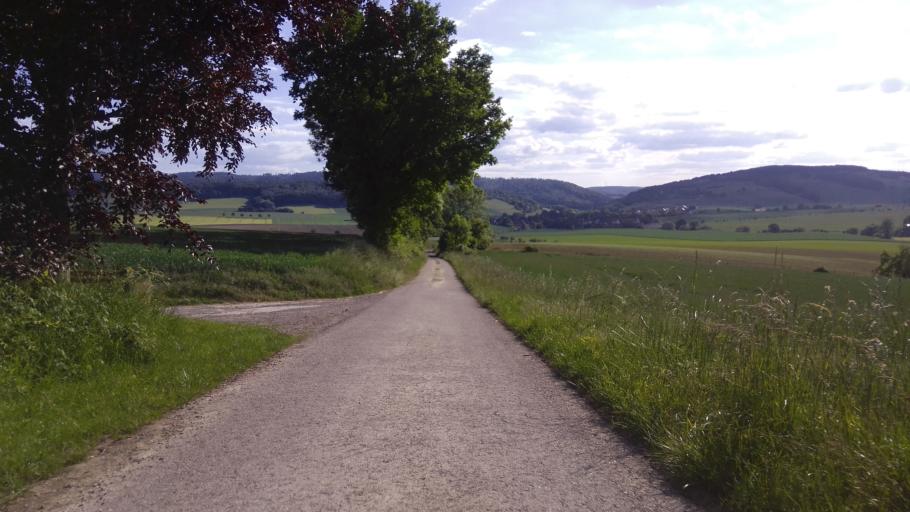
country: DE
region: Lower Saxony
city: Halle
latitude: 51.9989
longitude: 9.5867
